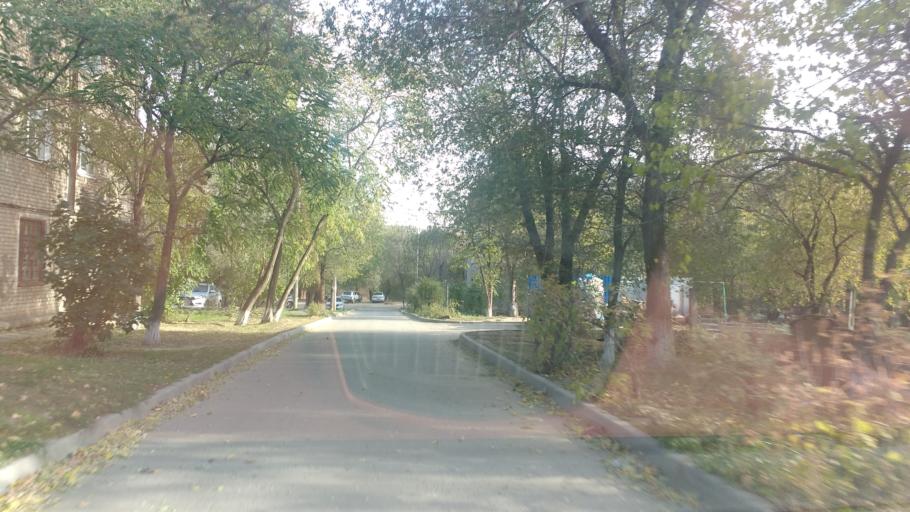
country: RU
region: Volgograd
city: Krasnoslobodsk
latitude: 48.7637
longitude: 44.5547
